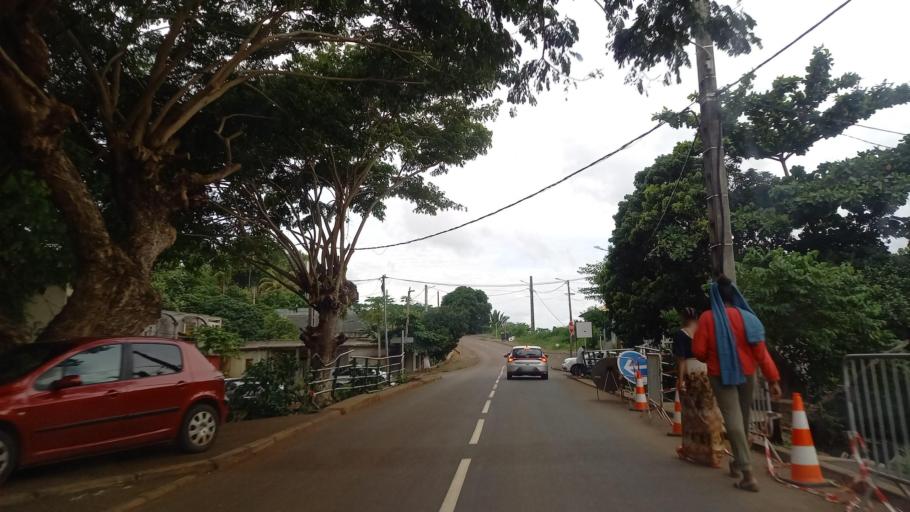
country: YT
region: Chirongui
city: Chirongui
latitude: -12.8935
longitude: 45.1416
